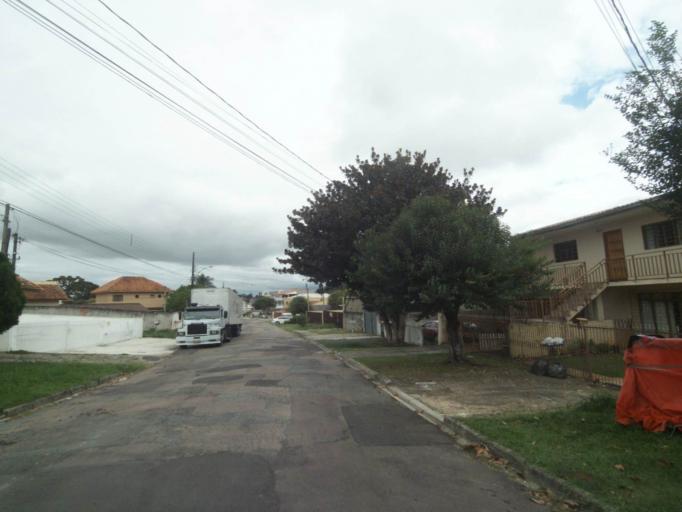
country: BR
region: Parana
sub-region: Curitiba
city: Curitiba
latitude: -25.4855
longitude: -49.2819
